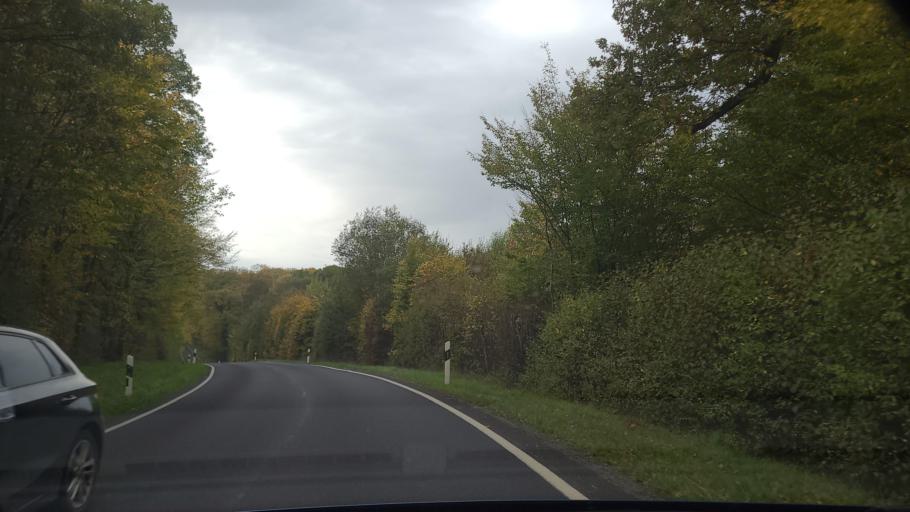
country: LU
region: Luxembourg
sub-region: Canton de Capellen
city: Mamer
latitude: 49.6112
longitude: 6.0082
